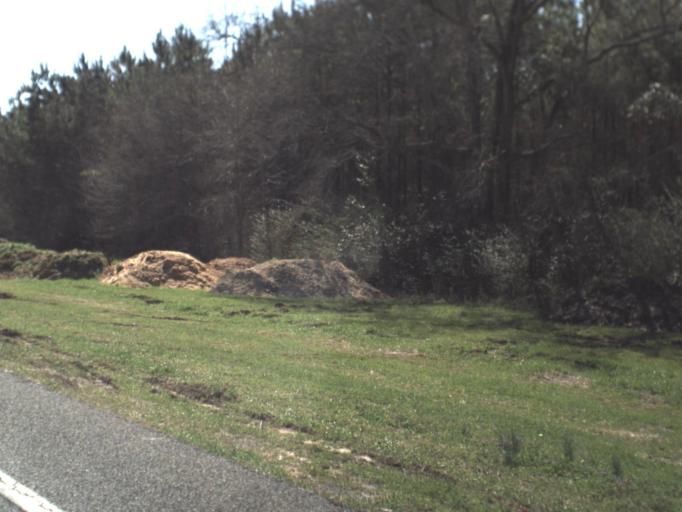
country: US
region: Florida
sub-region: Jackson County
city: Graceville
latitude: 30.9575
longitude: -85.4029
